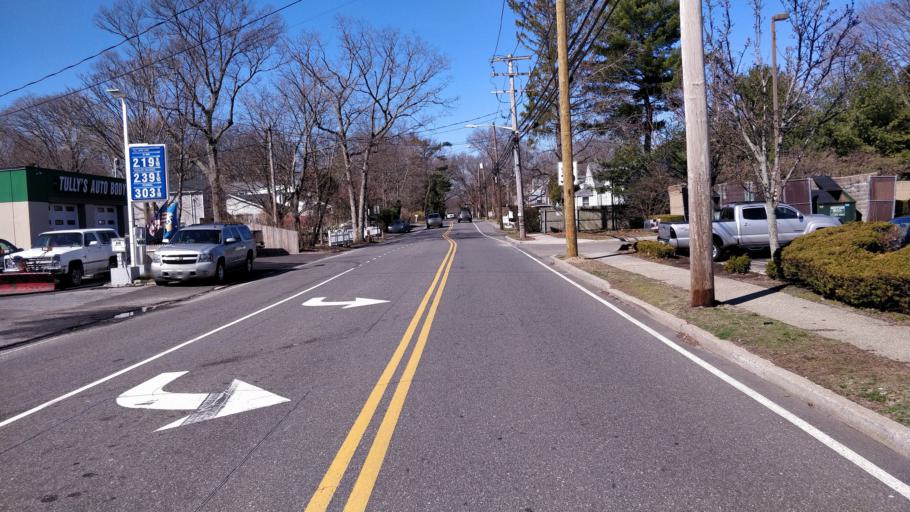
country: US
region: New York
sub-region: Suffolk County
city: Greenlawn
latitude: 40.8508
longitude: -73.3659
